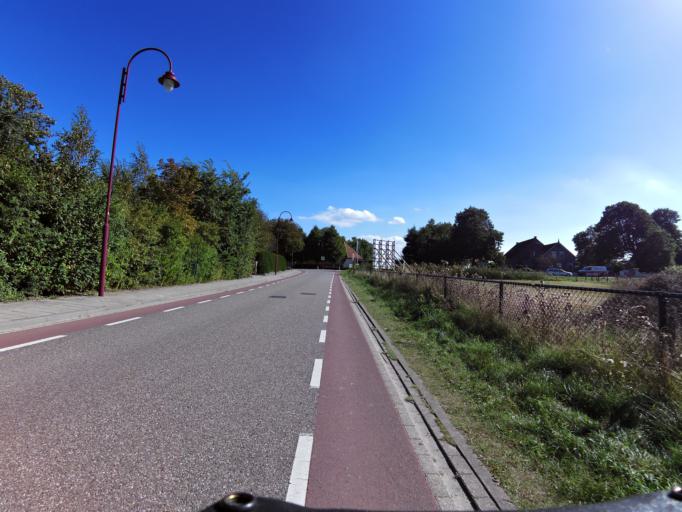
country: NL
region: South Holland
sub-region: Gemeente Goeree-Overflakkee
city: Ouddorp
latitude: 51.8069
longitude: 3.9362
